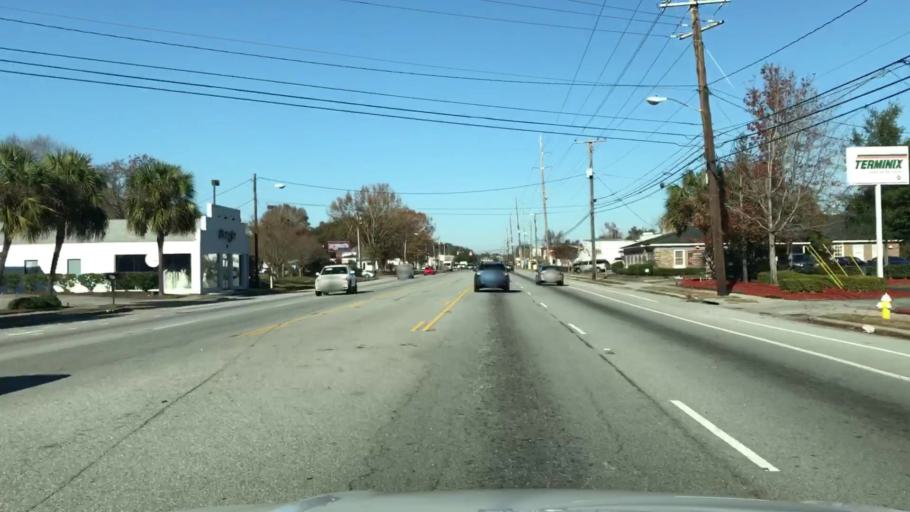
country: US
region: South Carolina
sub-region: Charleston County
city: Charleston
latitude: 32.7906
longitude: -79.9865
